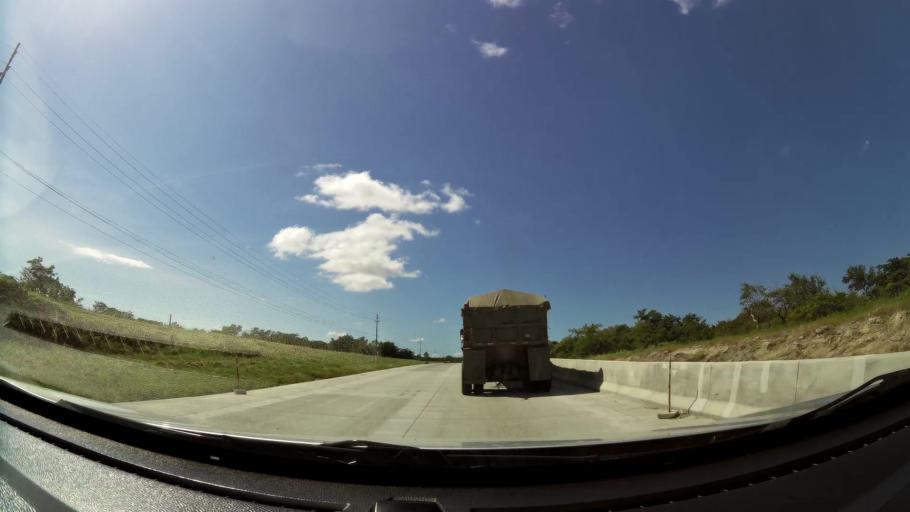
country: CR
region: Guanacaste
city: Bagaces
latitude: 10.5401
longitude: -85.3107
